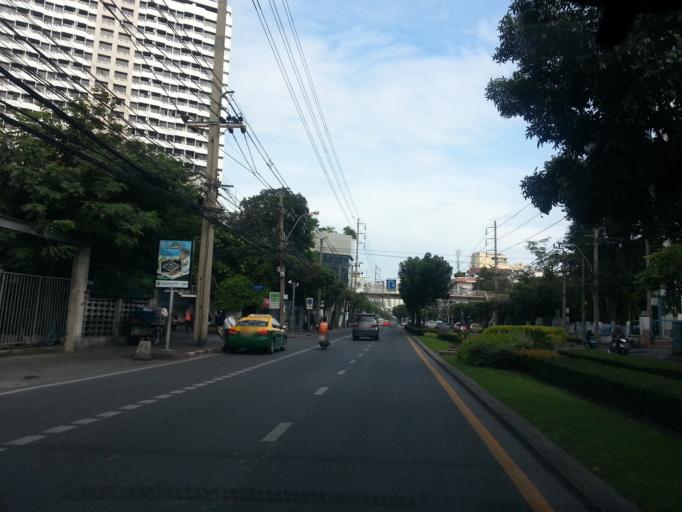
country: TH
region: Bangkok
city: Khlong Toei
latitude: 13.7167
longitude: 100.5726
